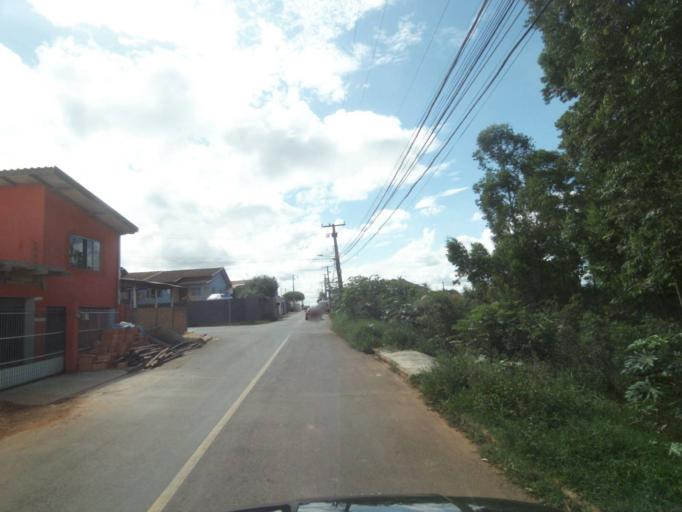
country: BR
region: Parana
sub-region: Telemaco Borba
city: Telemaco Borba
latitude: -24.3156
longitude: -50.6348
